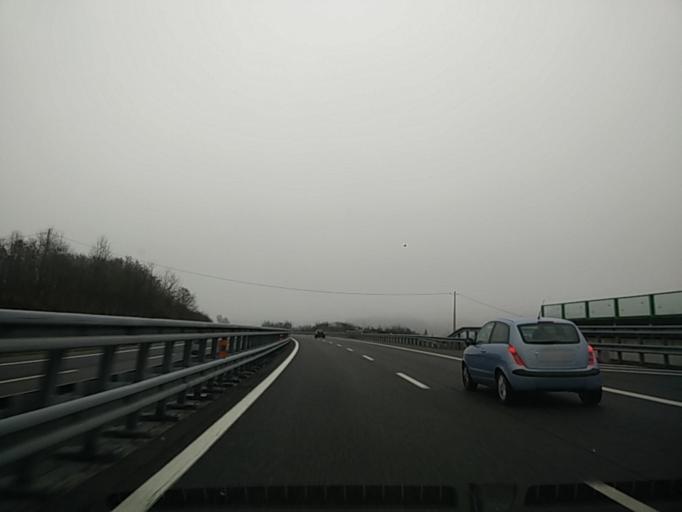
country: IT
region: Piedmont
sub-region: Provincia di Asti
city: Tigliole
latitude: 44.9033
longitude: 8.0593
